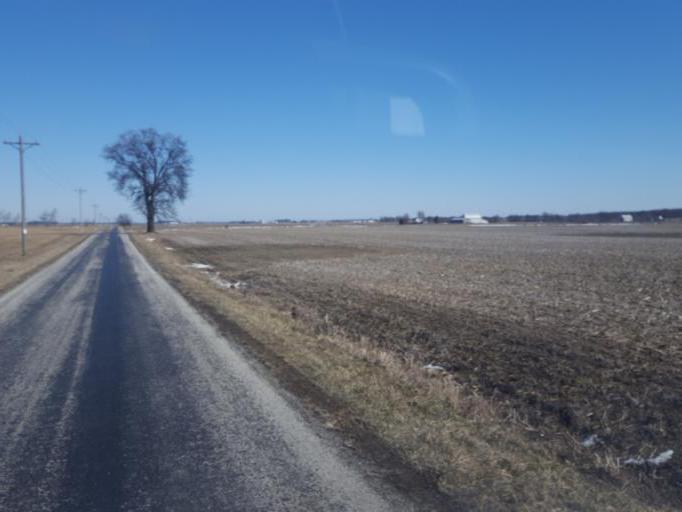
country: US
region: Ohio
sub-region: Marion County
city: Marion
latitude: 40.6512
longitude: -83.1979
